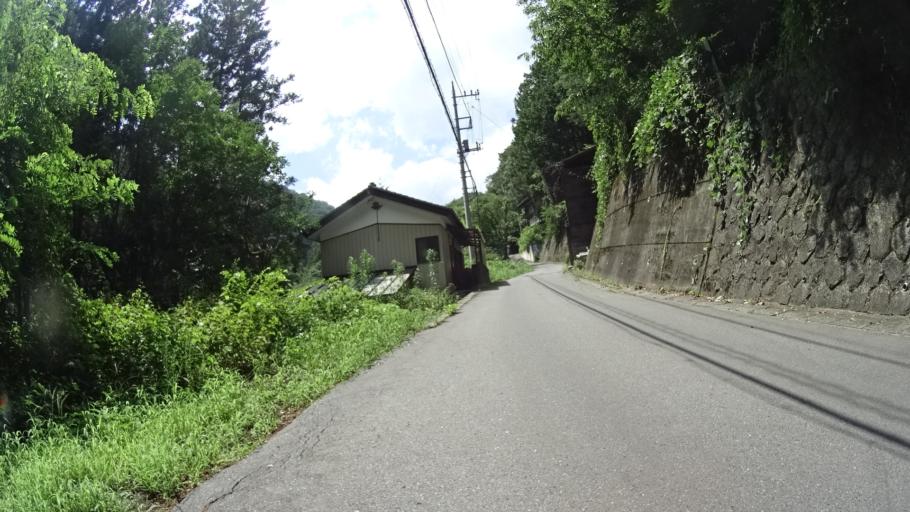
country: JP
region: Gunma
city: Tomioka
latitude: 36.0855
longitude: 138.7214
